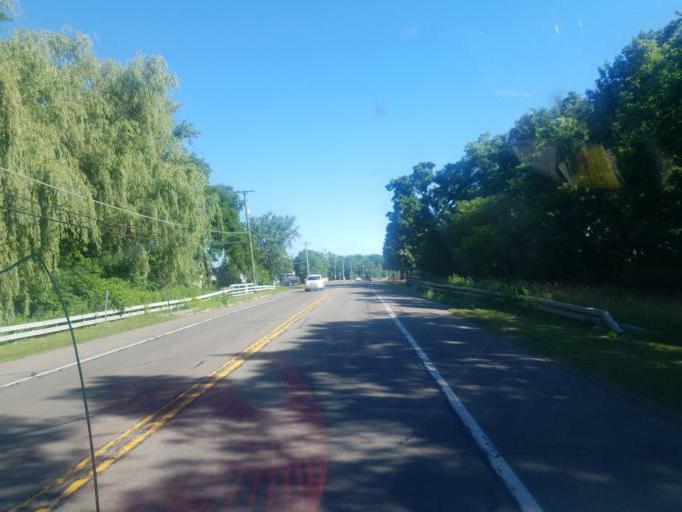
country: US
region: New York
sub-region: Ontario County
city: Canandaigua
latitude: 42.8704
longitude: -77.2509
